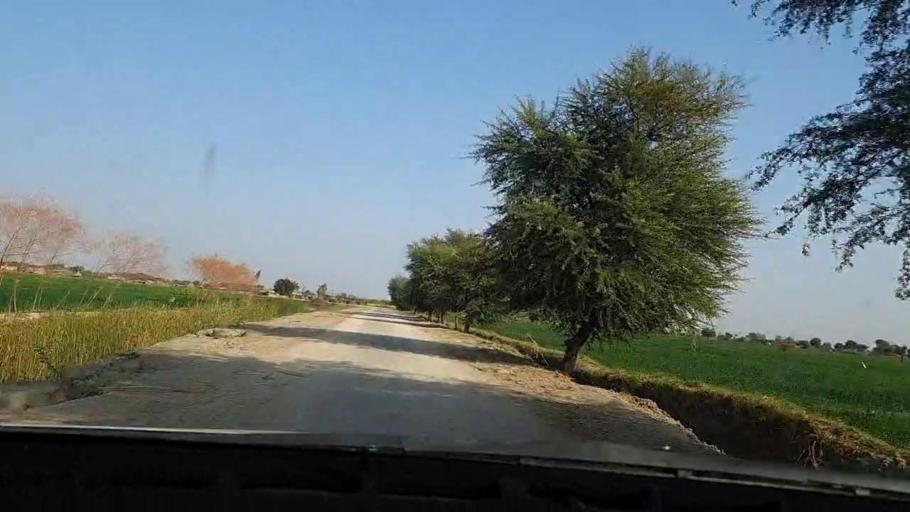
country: PK
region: Sindh
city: Tando Mittha Khan
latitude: 25.8298
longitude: 69.3144
